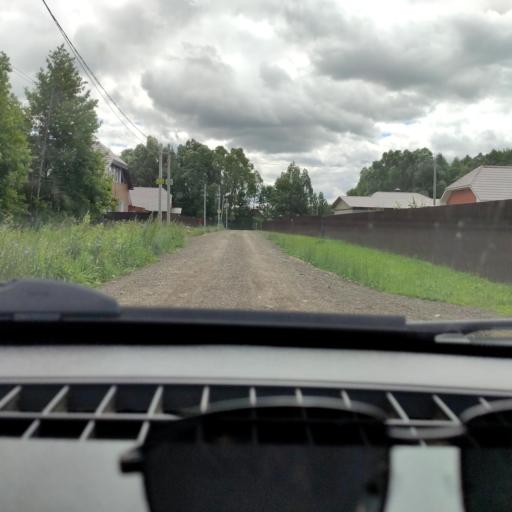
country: RU
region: Bashkortostan
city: Kabakovo
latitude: 54.6715
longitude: 56.0970
